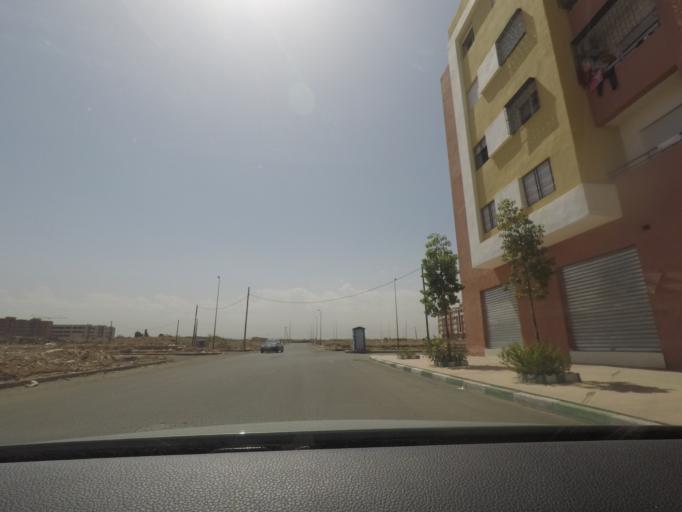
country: MA
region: Marrakech-Tensift-Al Haouz
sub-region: Marrakech
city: Marrakesh
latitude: 31.5853
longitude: -8.0384
